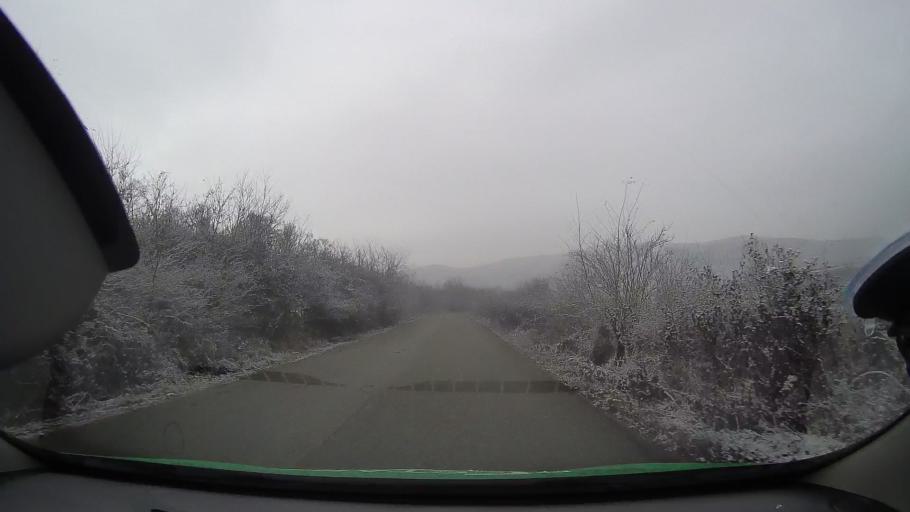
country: RO
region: Alba
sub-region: Comuna Hoparta
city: Hoparta
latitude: 46.3402
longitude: 23.9229
